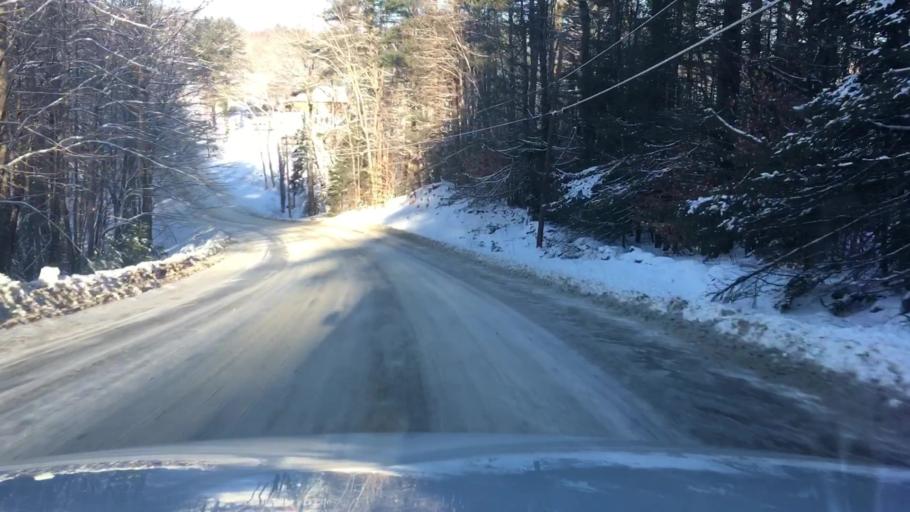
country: US
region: Maine
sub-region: Kennebec County
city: Readfield
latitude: 44.4181
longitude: -69.9227
